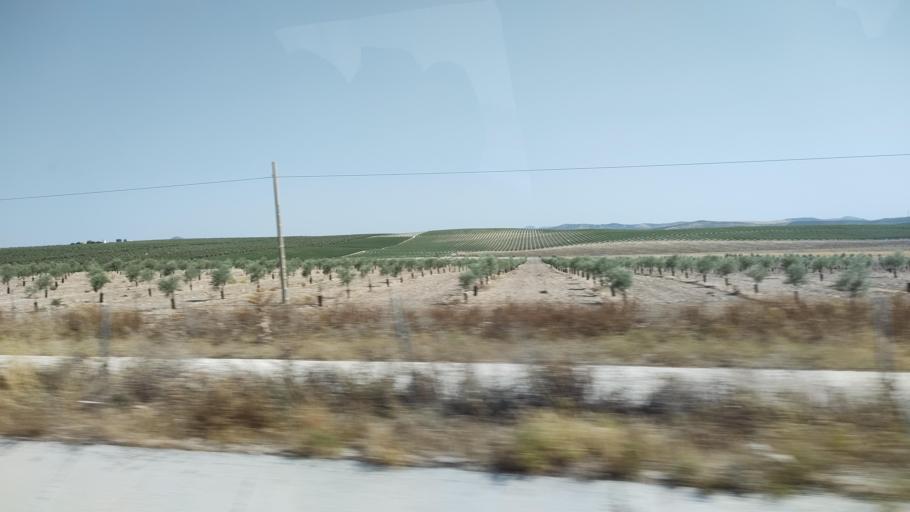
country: ES
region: Andalusia
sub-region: Provincia de Sevilla
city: La Puebla de Cazalla
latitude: 37.2319
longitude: -5.2312
